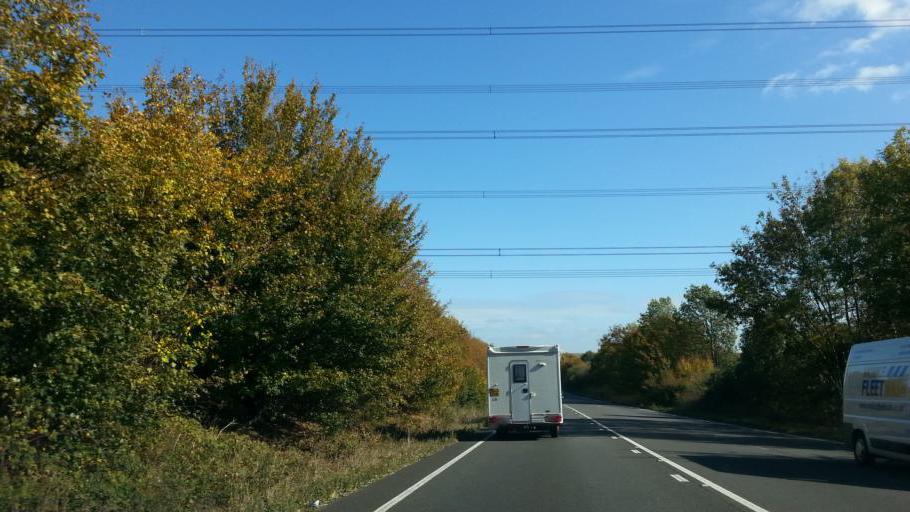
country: GB
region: England
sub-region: Peterborough
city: Castor
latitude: 52.5247
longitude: -0.3642
